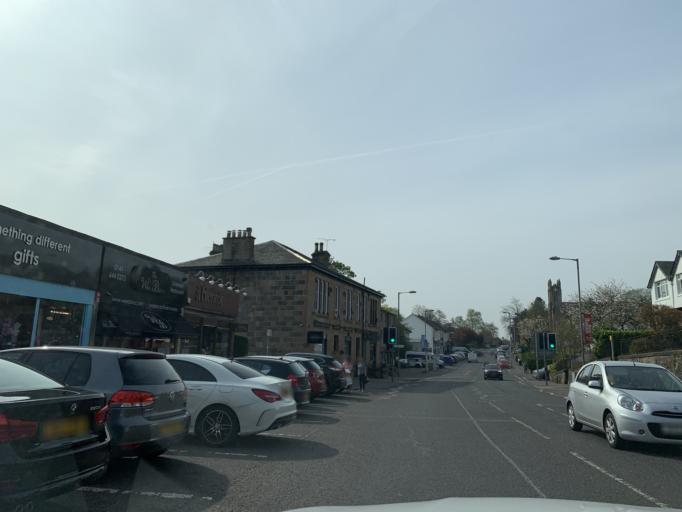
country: GB
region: Scotland
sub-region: East Renfrewshire
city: Clarkston
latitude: 55.7855
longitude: -4.2749
